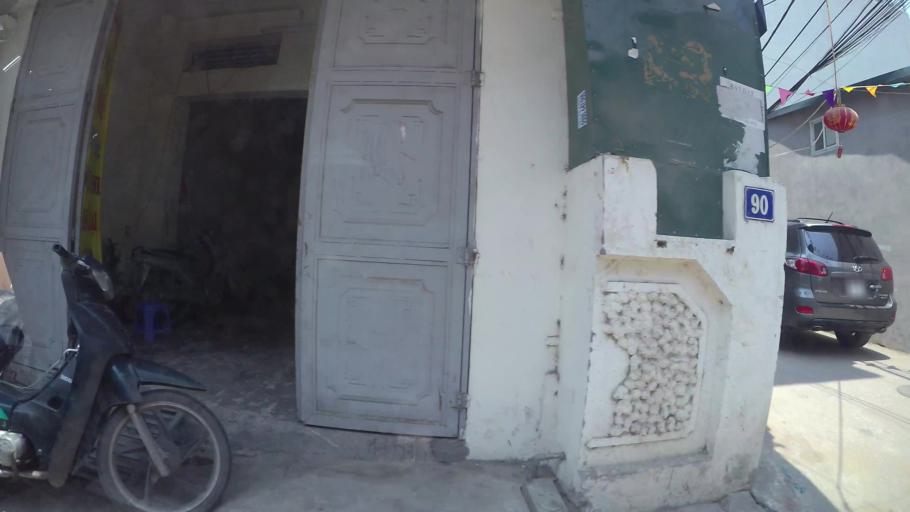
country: VN
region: Ha Noi
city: Hoan Kiem
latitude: 21.0233
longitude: 105.8921
